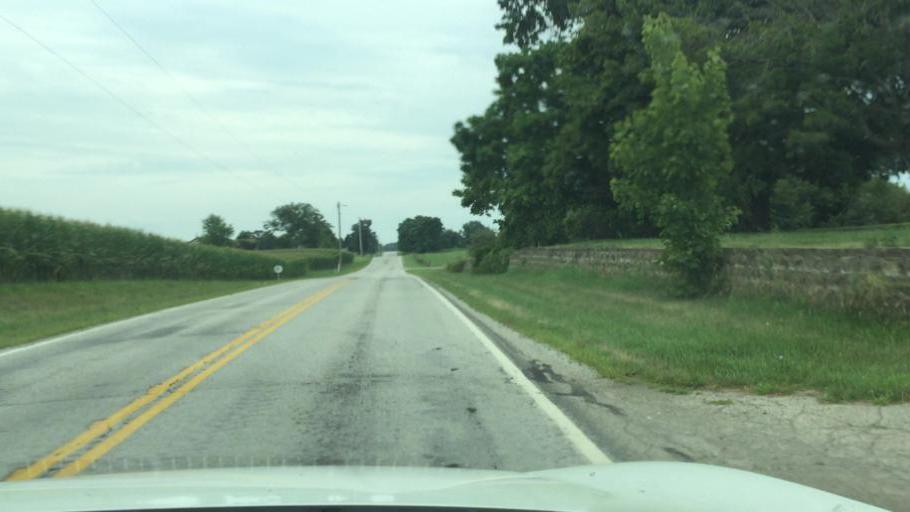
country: US
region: Ohio
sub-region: Clark County
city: Northridge
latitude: 39.9609
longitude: -83.6797
